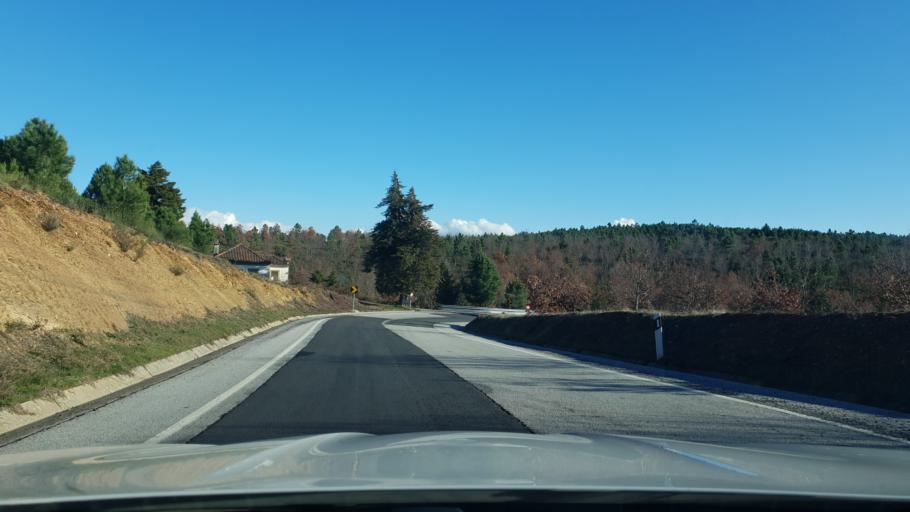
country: PT
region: Braganca
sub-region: Freixo de Espada A Cinta
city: Freixo de Espada a Cinta
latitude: 41.1385
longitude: -6.8063
